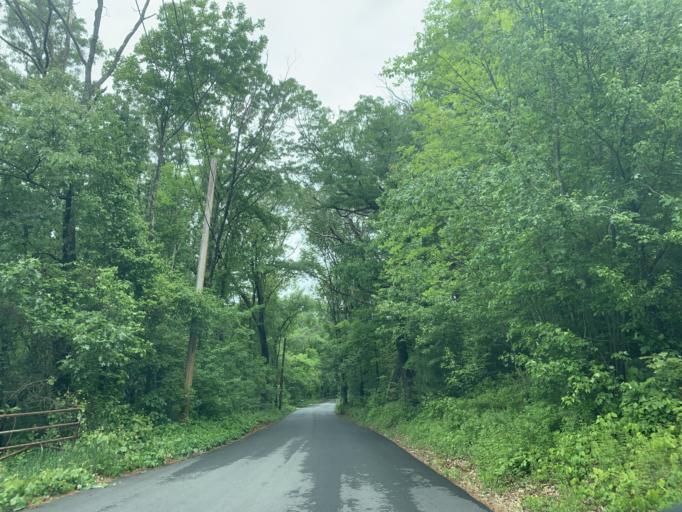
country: US
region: Massachusetts
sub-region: Worcester County
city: Upton
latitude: 42.1817
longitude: -71.6208
